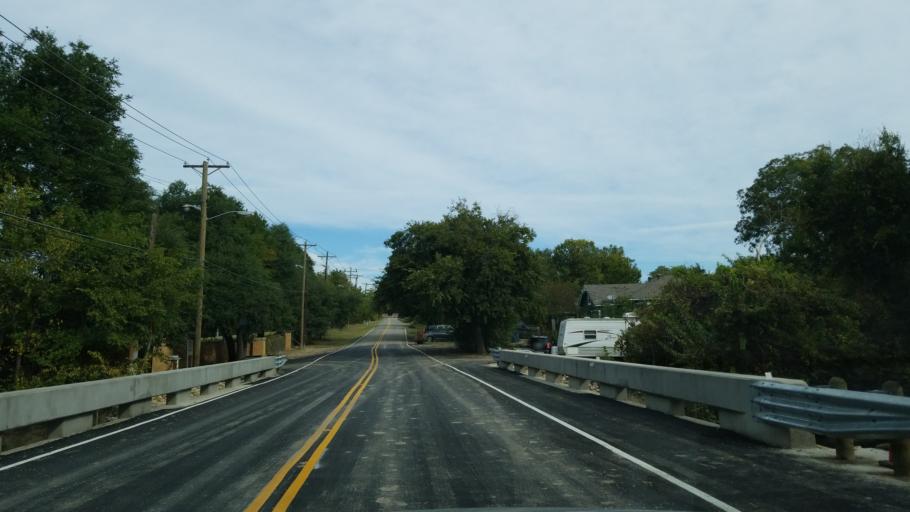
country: US
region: Texas
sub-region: Dallas County
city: Dallas
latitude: 32.7756
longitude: -96.7210
